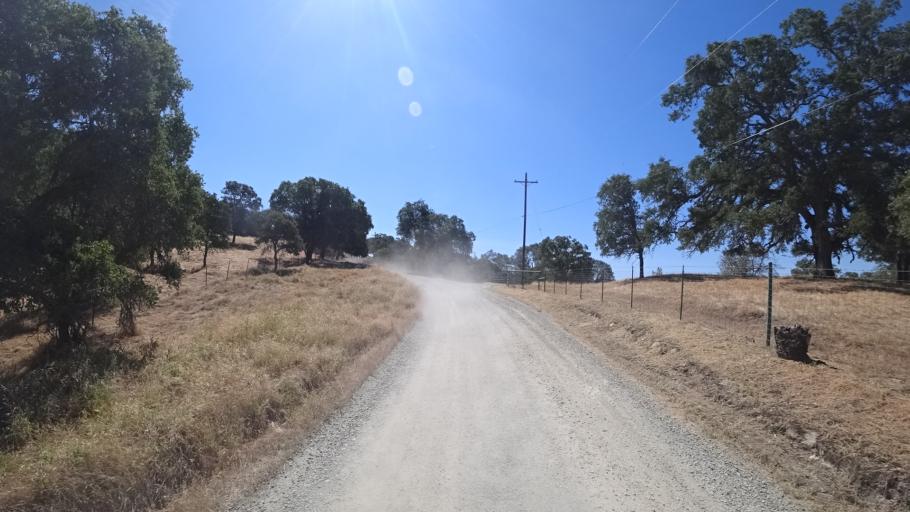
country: US
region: California
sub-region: Calaveras County
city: Valley Springs
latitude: 38.2178
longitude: -120.8719
